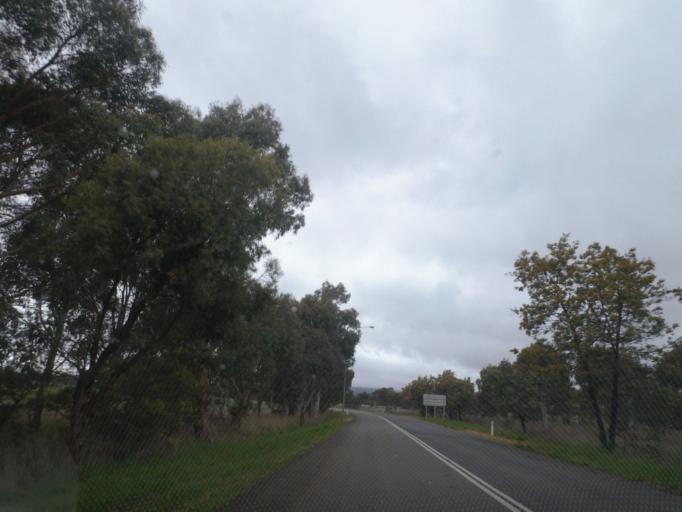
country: AU
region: Victoria
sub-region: Hume
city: Sunbury
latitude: -37.3194
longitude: 144.5287
